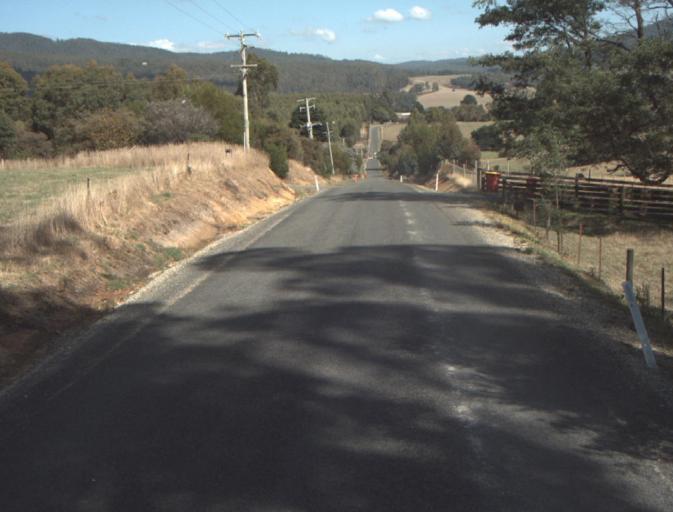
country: AU
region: Tasmania
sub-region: Launceston
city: Mayfield
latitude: -41.2338
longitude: 147.2348
